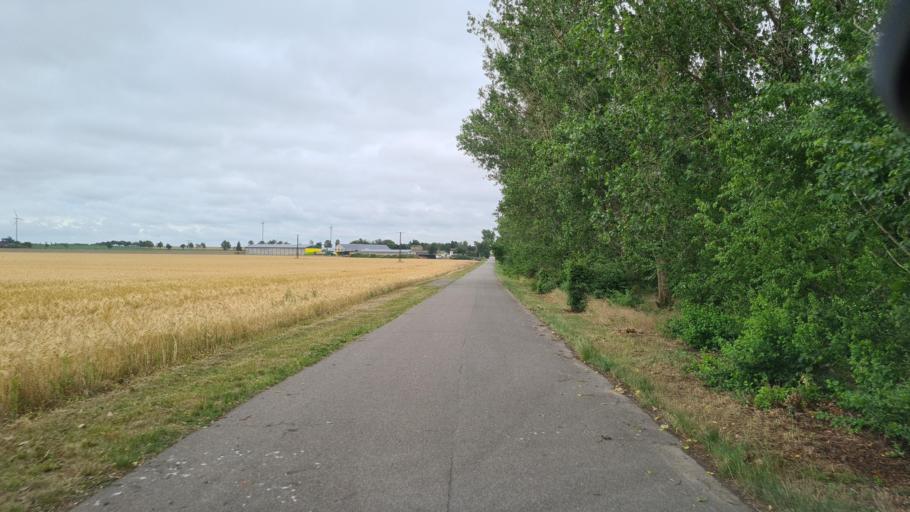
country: DE
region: Brandenburg
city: Juterbog
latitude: 51.9402
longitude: 13.1917
